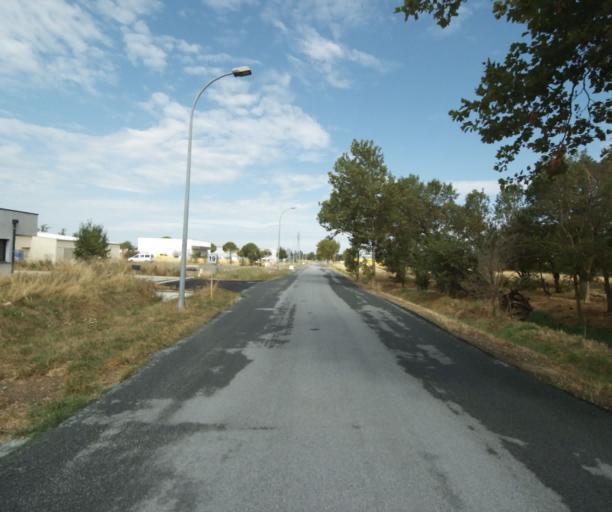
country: FR
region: Midi-Pyrenees
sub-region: Departement de la Haute-Garonne
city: Revel
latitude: 43.4581
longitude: 1.9833
